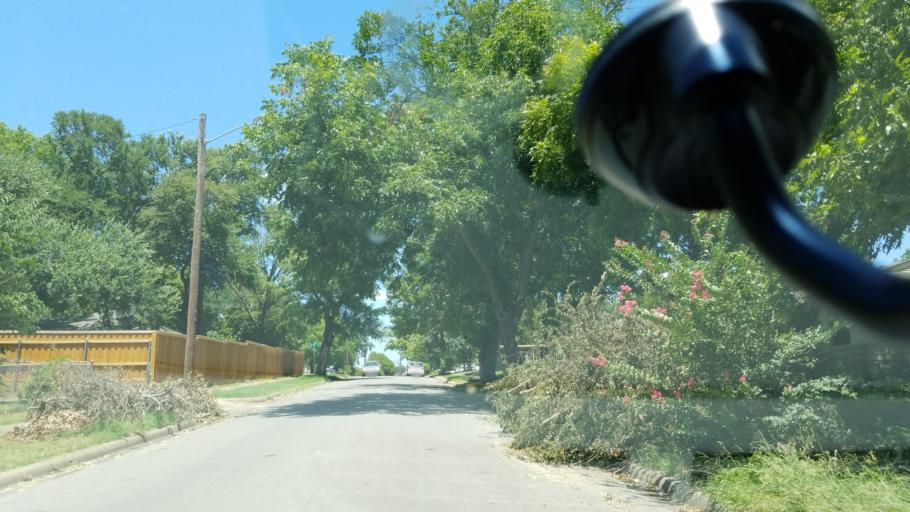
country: US
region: Texas
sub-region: Dallas County
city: Cockrell Hill
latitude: 32.6878
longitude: -96.8130
